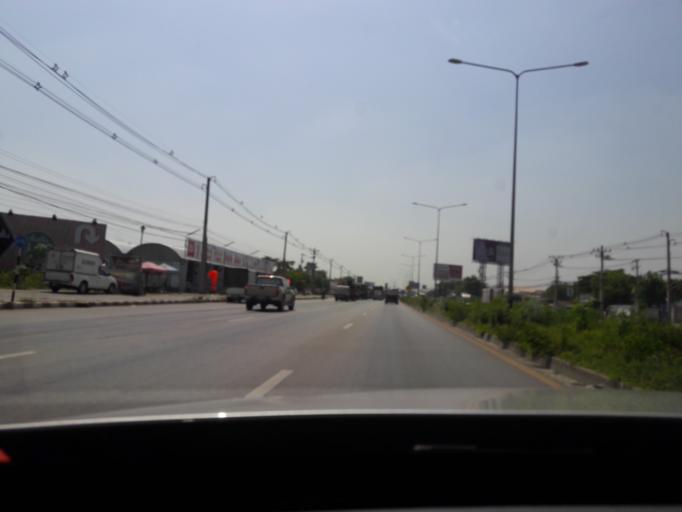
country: TH
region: Bangkok
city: Nong Khaem
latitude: 13.6857
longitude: 100.3238
